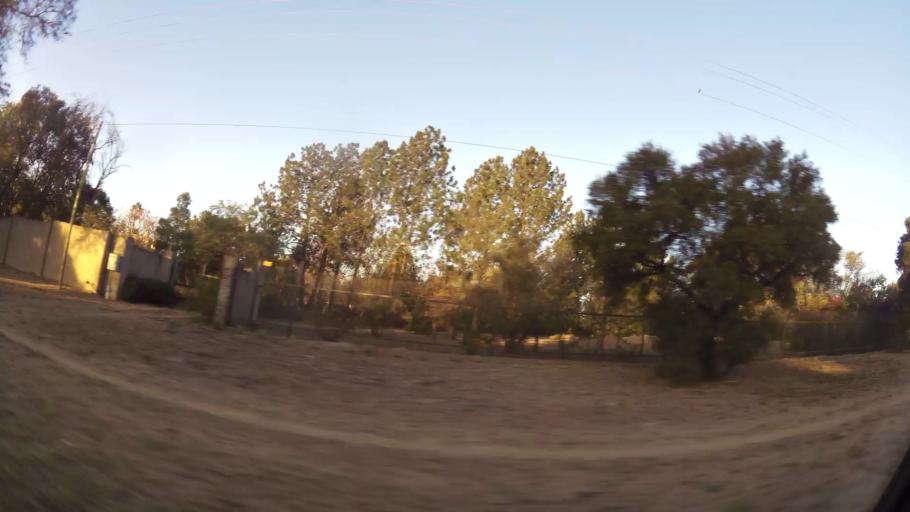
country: ZA
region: Gauteng
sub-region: City of Johannesburg Metropolitan Municipality
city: Diepsloot
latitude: -25.9654
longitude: 28.0469
